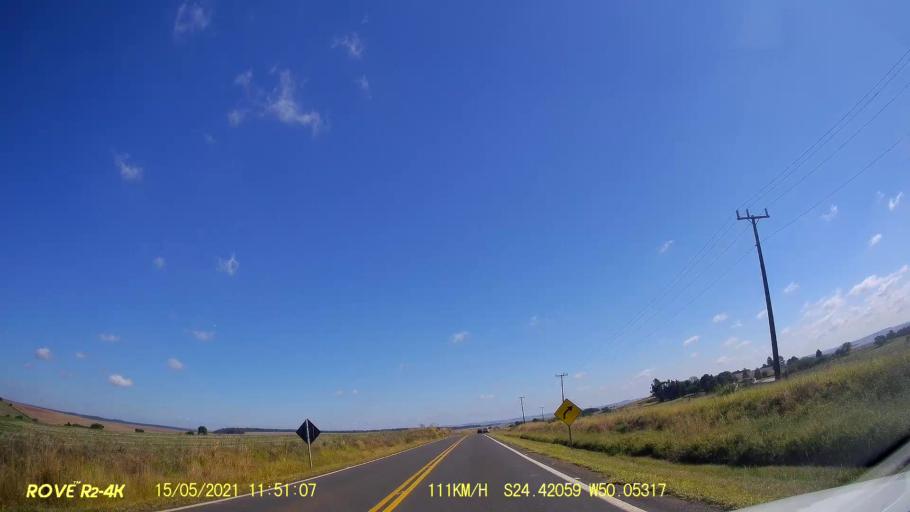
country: BR
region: Parana
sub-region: Pirai Do Sul
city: Pirai do Sul
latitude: -24.4205
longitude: -50.0533
